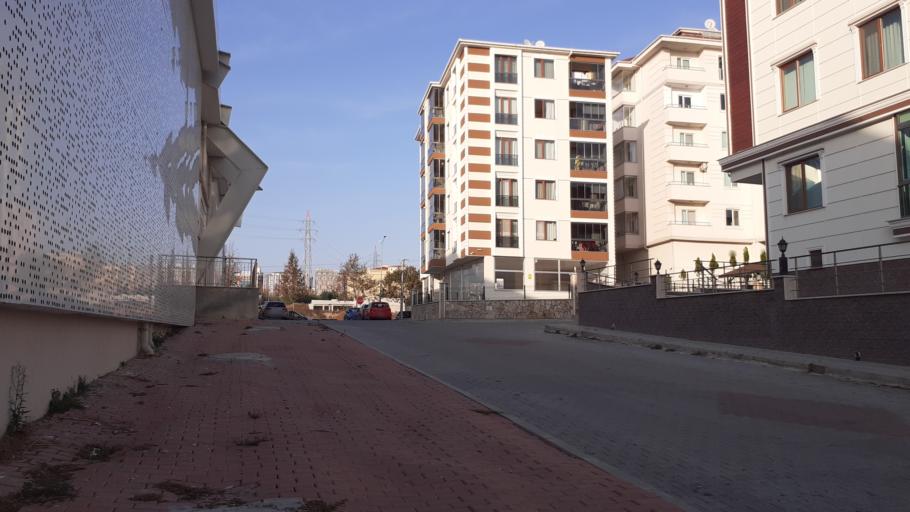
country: TR
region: Tekirdag
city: Corlu
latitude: 41.1484
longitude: 27.8283
